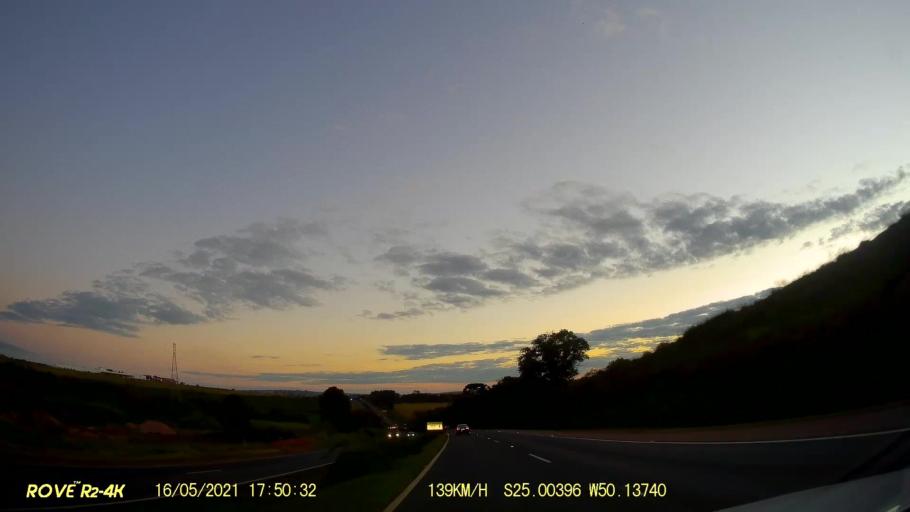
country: BR
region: Parana
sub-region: Carambei
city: Carambei
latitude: -25.0040
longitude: -50.1374
